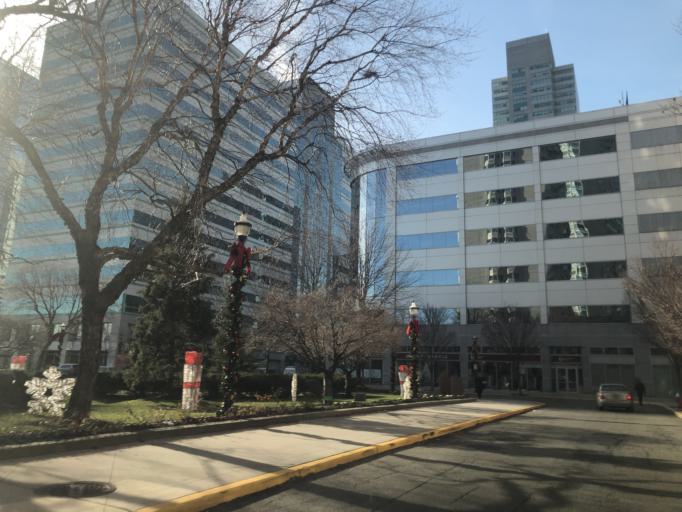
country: US
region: New Jersey
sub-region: Hudson County
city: Hoboken
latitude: 40.7269
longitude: -74.0322
